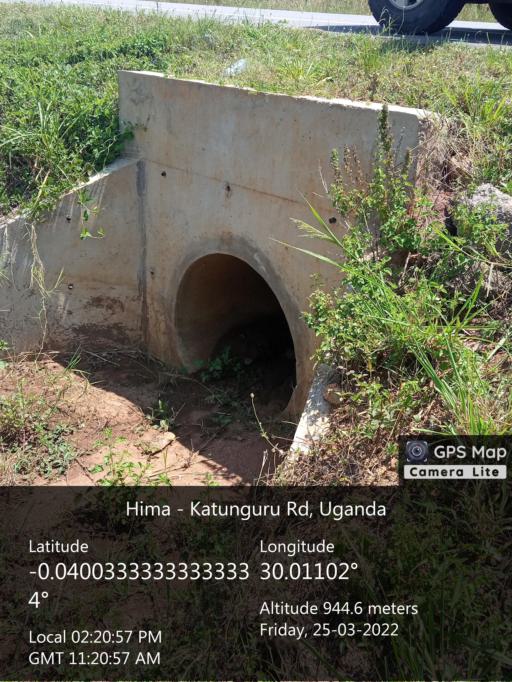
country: UG
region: Western Region
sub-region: Kasese District
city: Kasese
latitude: -0.0400
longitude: 30.0110
